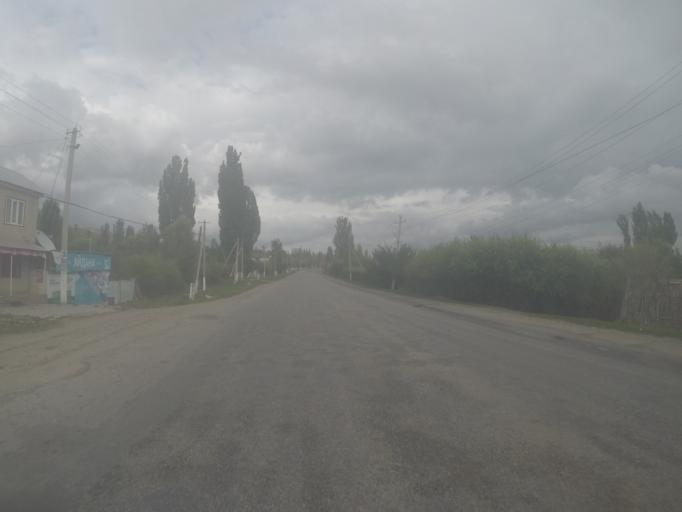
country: KG
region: Ysyk-Koel
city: Tyup
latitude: 42.7473
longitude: 78.0878
